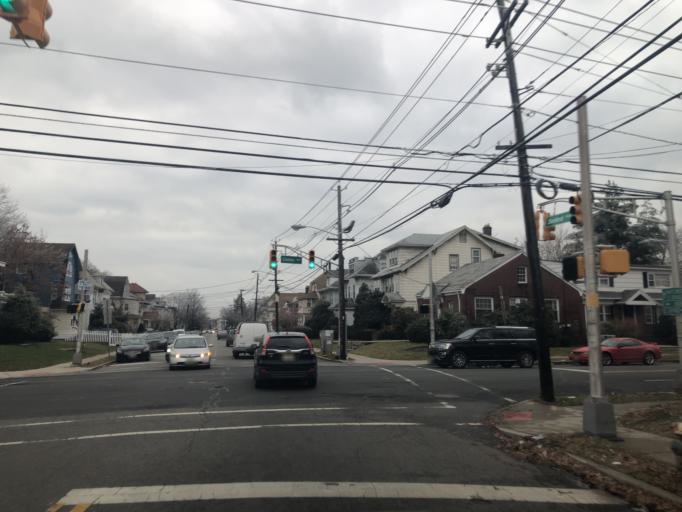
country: US
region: New Jersey
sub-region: Essex County
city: Irvington
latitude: 40.7297
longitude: -74.2402
